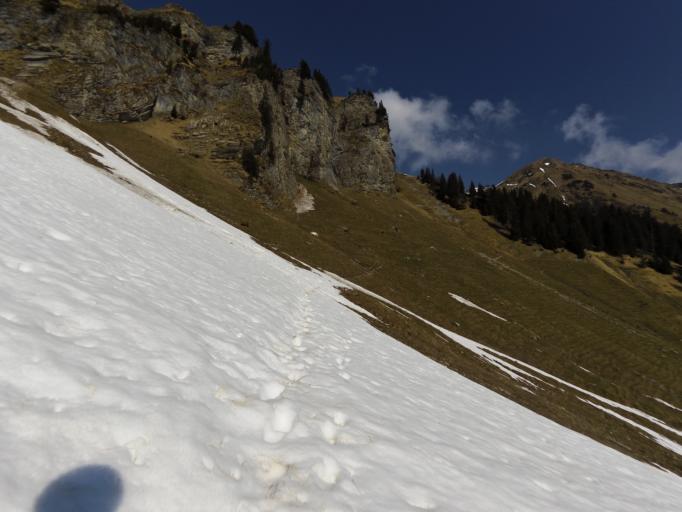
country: CH
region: Nidwalden
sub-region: Nidwalden
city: Emmetten
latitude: 46.9046
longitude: 8.4970
